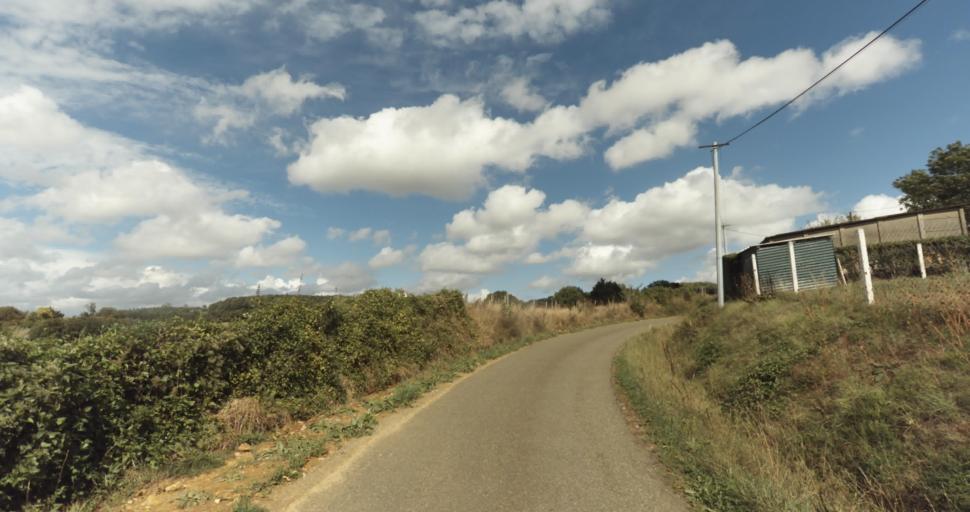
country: FR
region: Lower Normandy
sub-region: Departement de l'Orne
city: Gace
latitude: 48.7737
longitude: 0.3092
